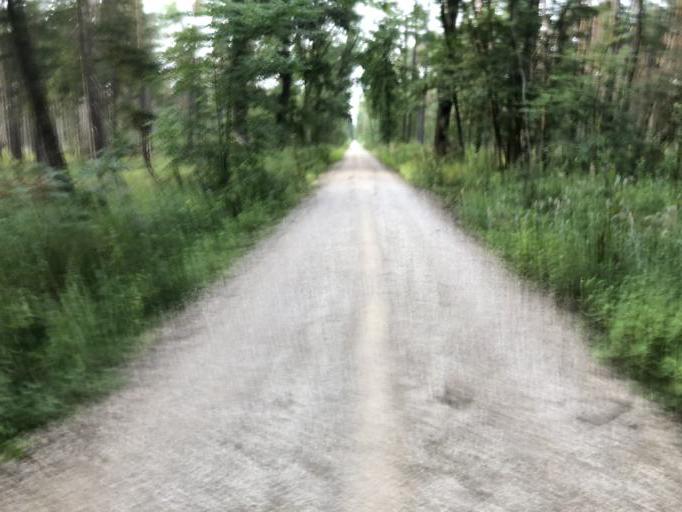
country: DE
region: Bavaria
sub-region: Regierungsbezirk Mittelfranken
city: Uttenreuth
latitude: 49.5767
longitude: 11.0767
